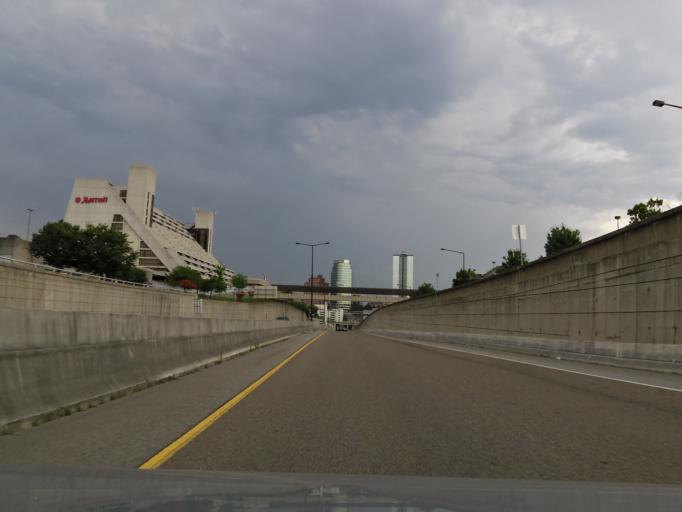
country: US
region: Tennessee
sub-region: Knox County
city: Knoxville
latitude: 35.9657
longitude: -83.9082
